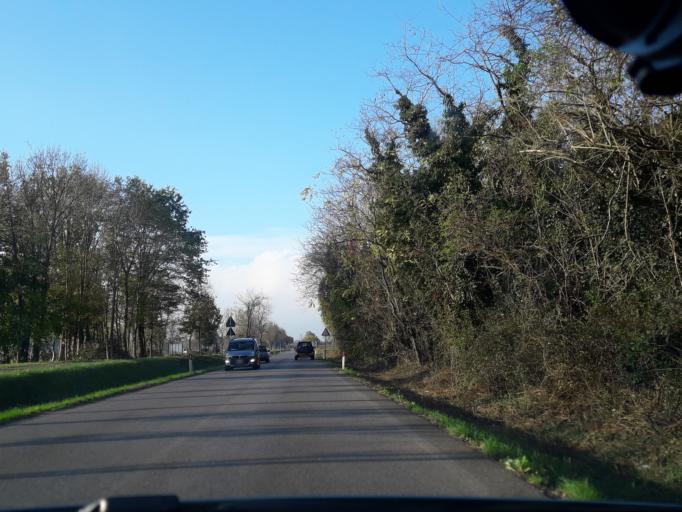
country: IT
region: Friuli Venezia Giulia
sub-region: Provincia di Udine
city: Pradamano
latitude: 46.0377
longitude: 13.2924
